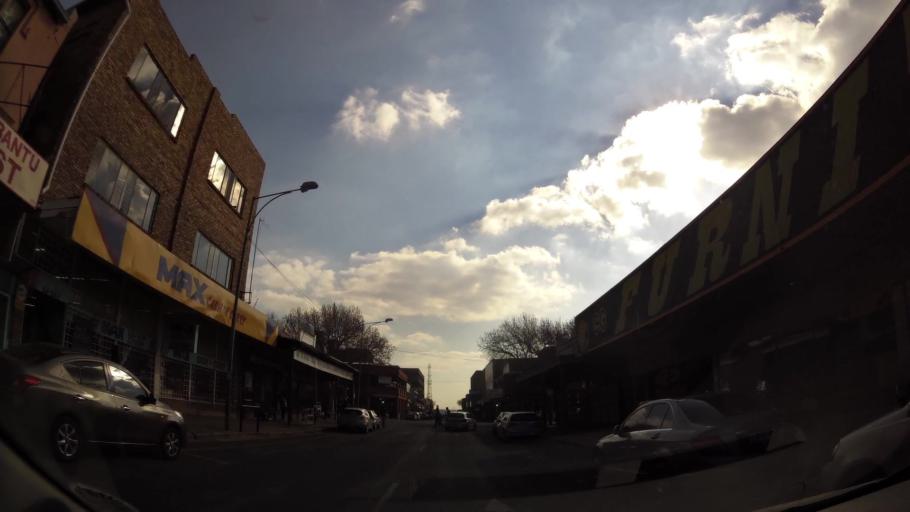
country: ZA
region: Gauteng
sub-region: West Rand District Municipality
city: Krugersdorp
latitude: -26.1029
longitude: 27.7736
